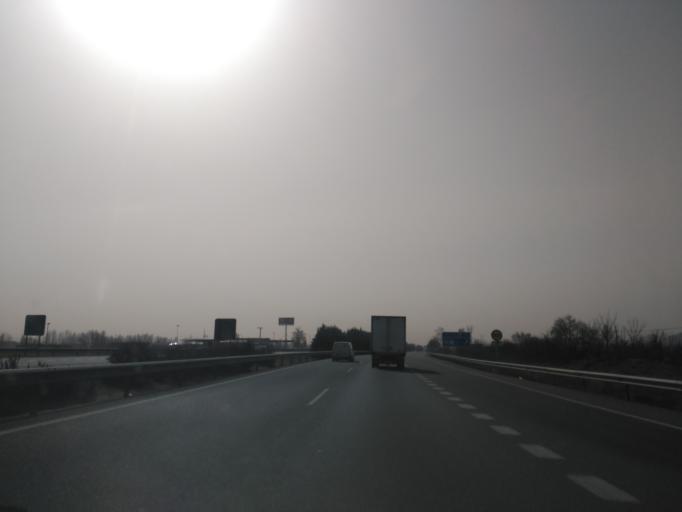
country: ES
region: Castille and Leon
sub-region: Provincia de Palencia
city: Venta de Banos
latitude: 41.9169
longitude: -4.5097
